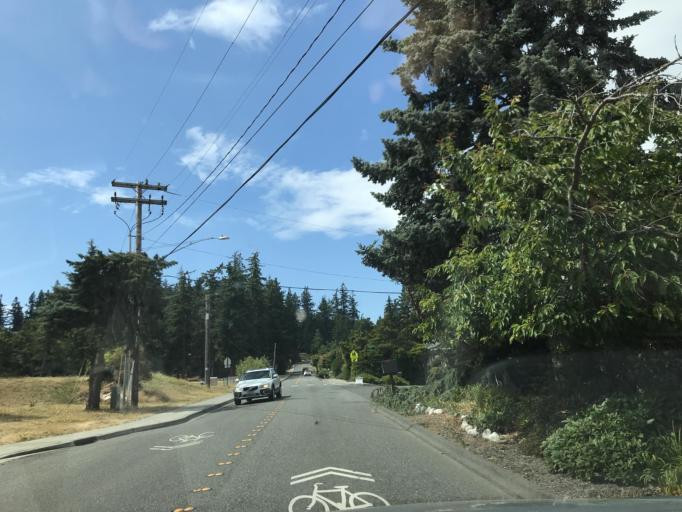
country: US
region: Washington
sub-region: Whatcom County
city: Bellingham
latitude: 48.7150
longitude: -122.5041
